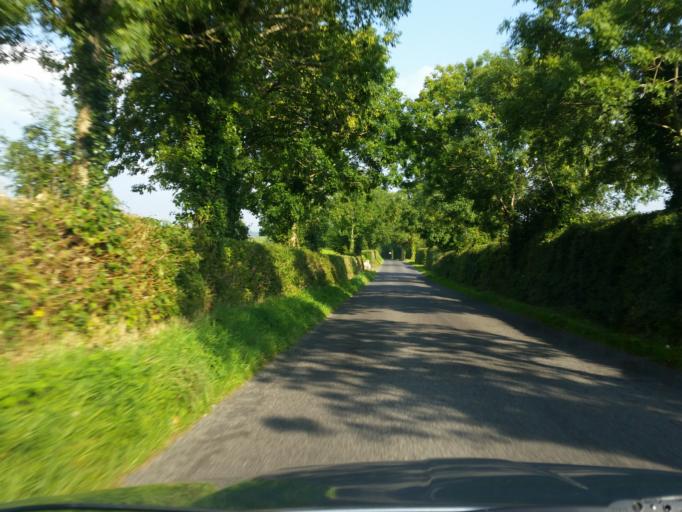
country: GB
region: Northern Ireland
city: Lisnaskea
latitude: 54.2880
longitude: -7.4556
